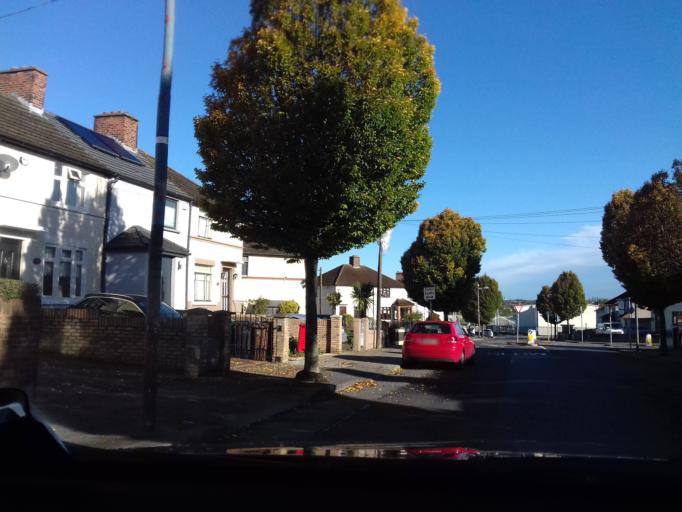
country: IE
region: Leinster
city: Cabra
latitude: 53.3707
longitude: -6.3006
